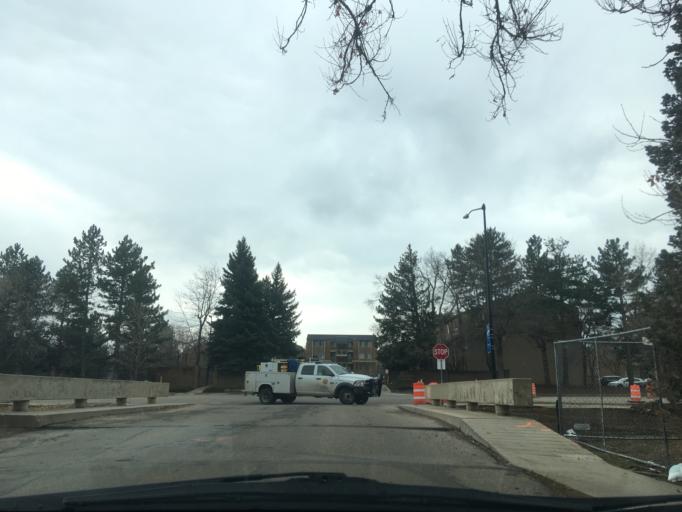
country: US
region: Colorado
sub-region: Boulder County
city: Boulder
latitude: 40.0078
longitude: -105.2517
